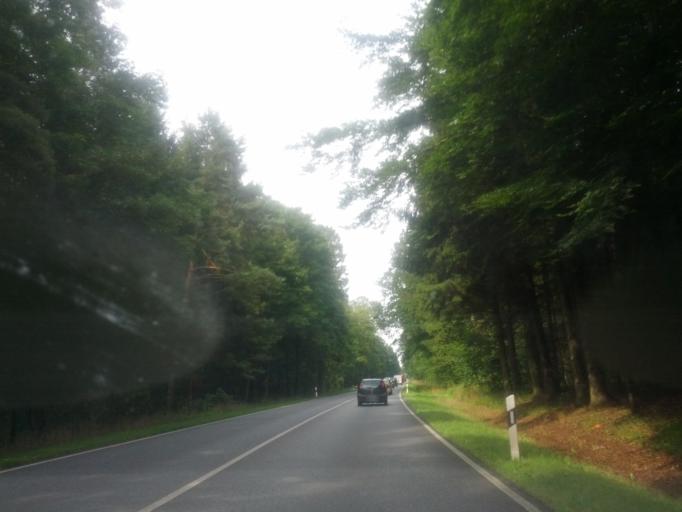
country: DE
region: Mecklenburg-Vorpommern
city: Neubukow
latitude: 54.0087
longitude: 11.6443
